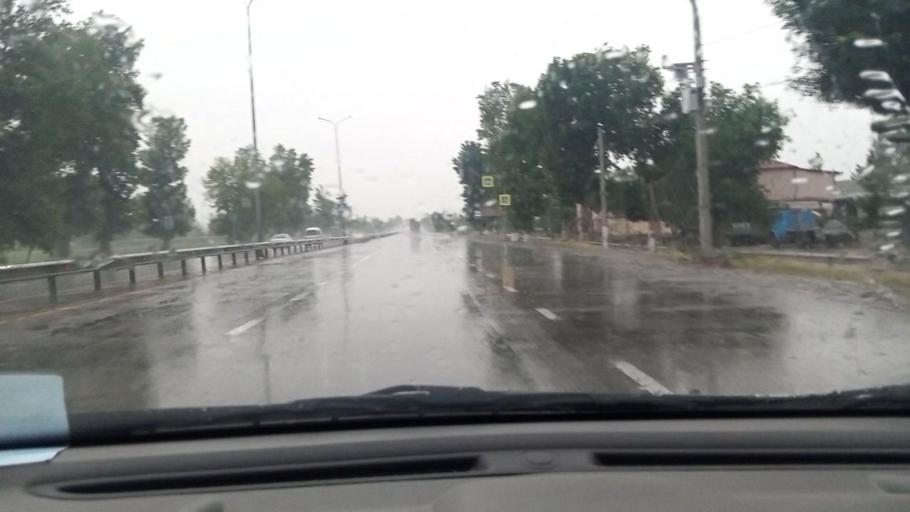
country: UZ
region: Toshkent Shahri
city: Bektemir
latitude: 41.1551
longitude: 69.4243
